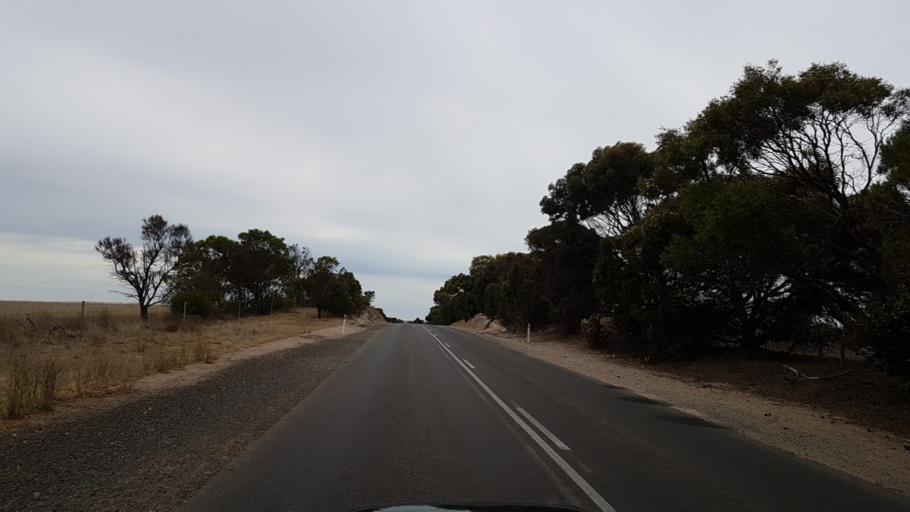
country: AU
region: South Australia
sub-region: Yorke Peninsula
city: Honiton
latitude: -34.9850
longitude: 137.2727
